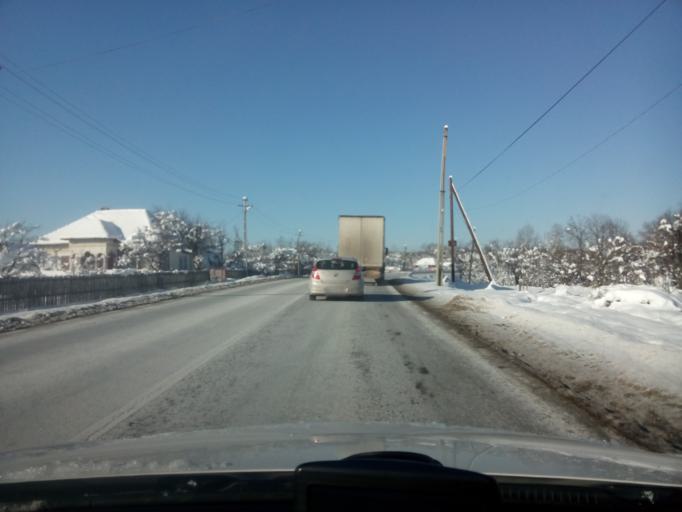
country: RO
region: Arges
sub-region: Comuna Cotmeana
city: Cotmeana
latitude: 44.9837
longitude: 24.6497
